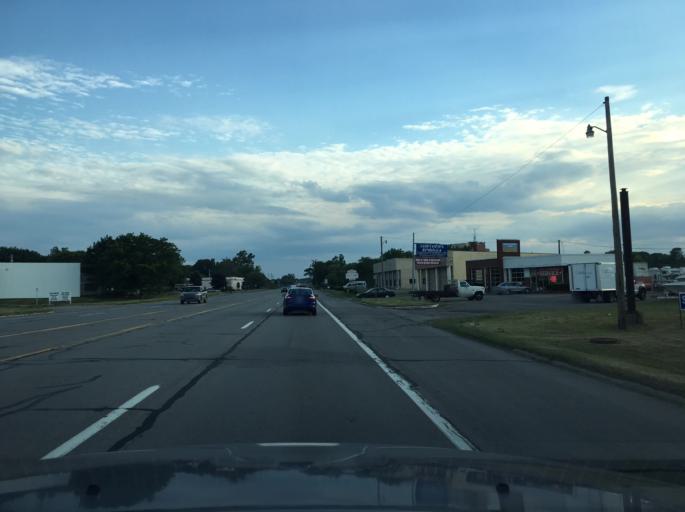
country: US
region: Michigan
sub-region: Macomb County
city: Mount Clemens
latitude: 42.6203
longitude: -82.8813
